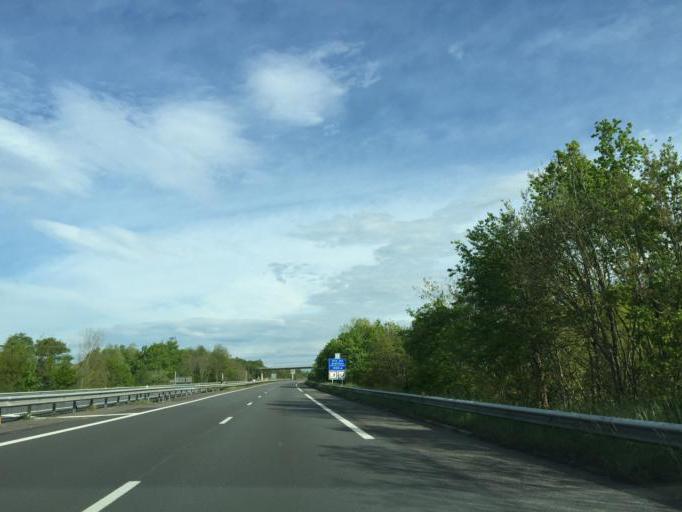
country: FR
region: Rhone-Alpes
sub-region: Departement de la Loire
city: Balbigny
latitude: 45.8299
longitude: 4.1026
